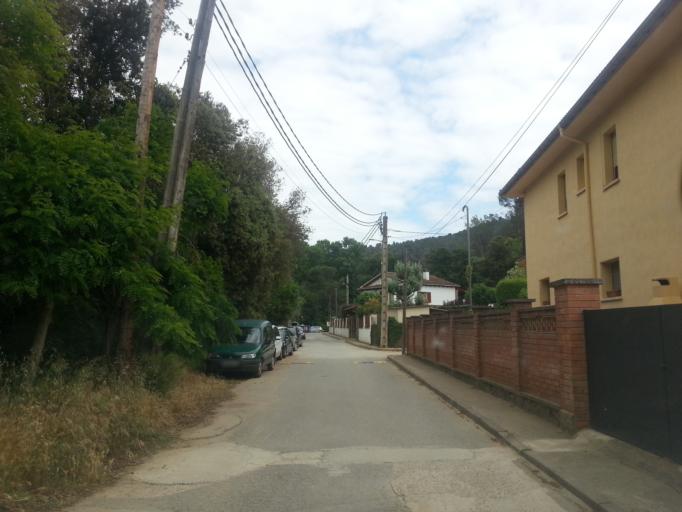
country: ES
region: Catalonia
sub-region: Provincia de Barcelona
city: Molins de Rei
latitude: 41.4360
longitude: 2.0430
